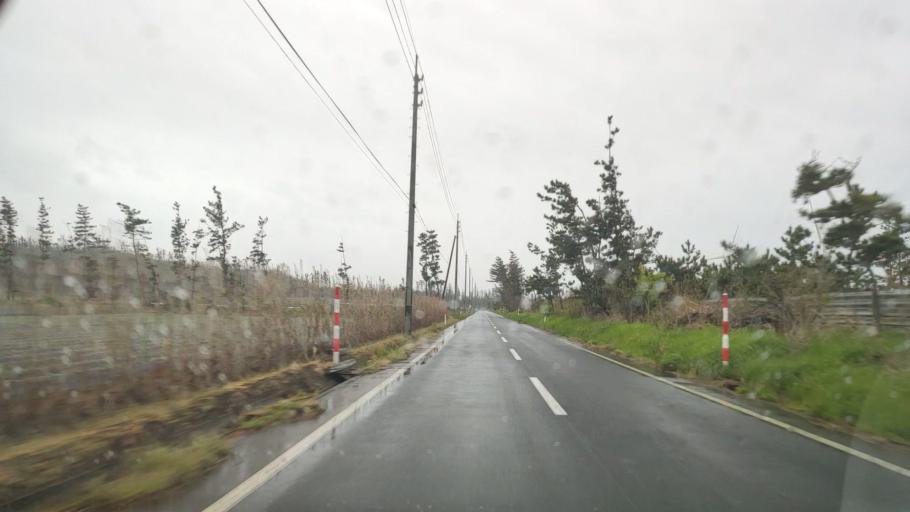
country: JP
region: Akita
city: Noshiromachi
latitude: 40.0847
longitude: 139.9575
